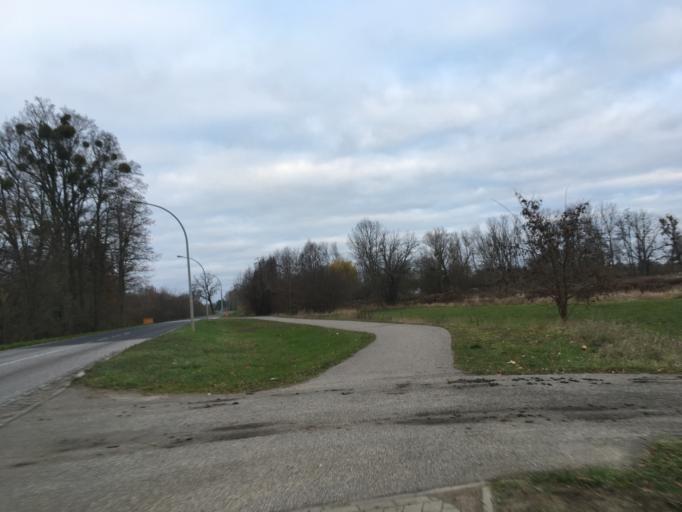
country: DE
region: Brandenburg
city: Seelow
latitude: 52.5751
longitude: 14.3485
